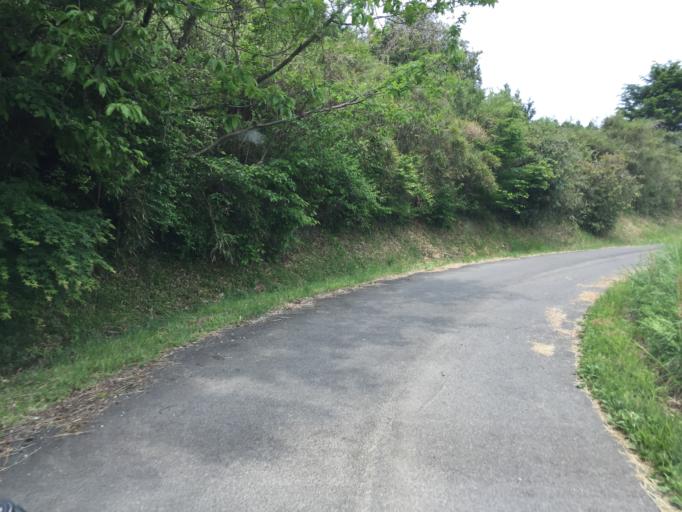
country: JP
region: Fukushima
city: Fukushima-shi
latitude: 37.7080
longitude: 140.3469
